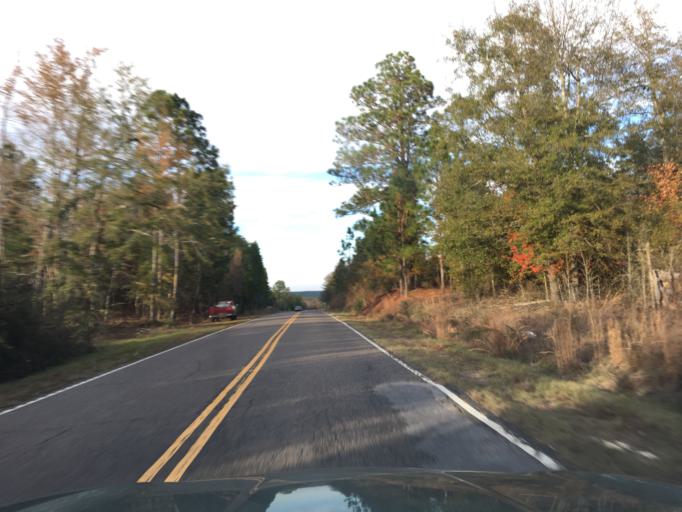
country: US
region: South Carolina
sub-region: Lexington County
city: Red Bank
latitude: 33.7100
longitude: -81.3557
